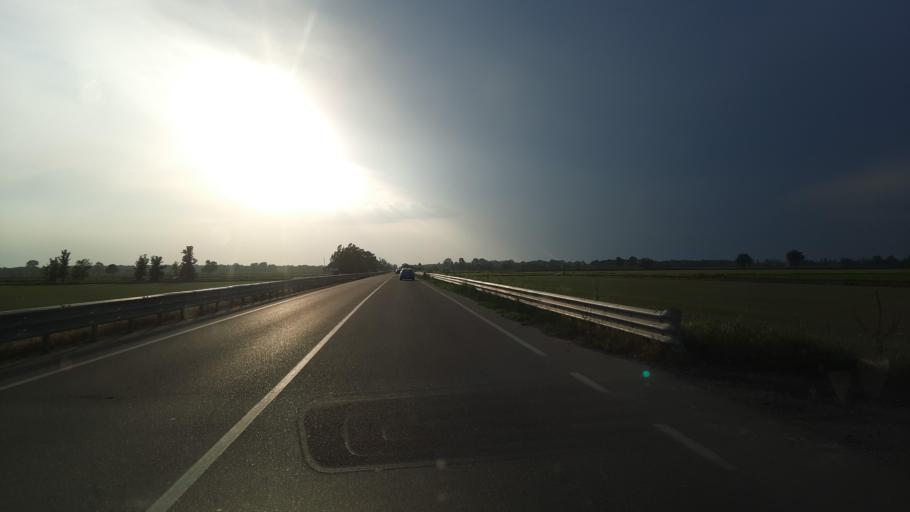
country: IT
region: Lombardy
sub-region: Provincia di Pavia
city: Tromello
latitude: 45.2226
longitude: 8.8370
